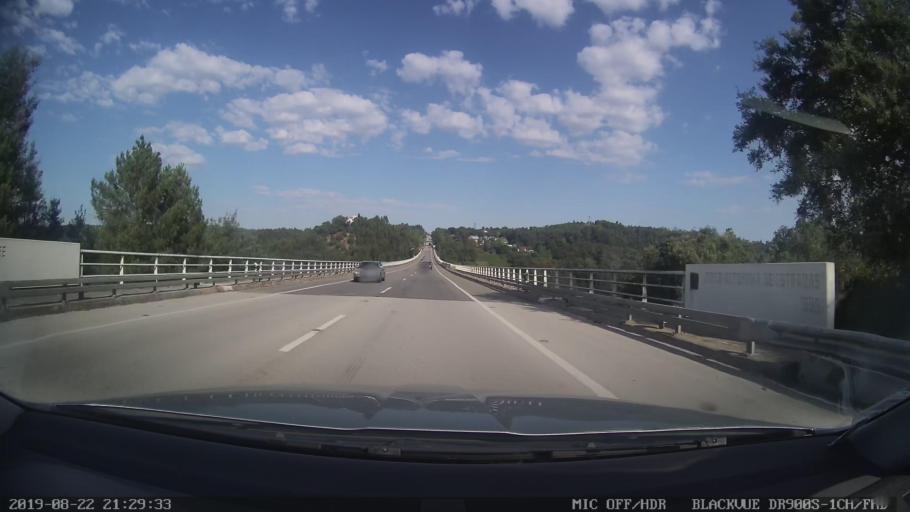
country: PT
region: Leiria
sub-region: Pedrogao Grande
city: Pedrogao Grande
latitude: 39.9032
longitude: -8.1371
